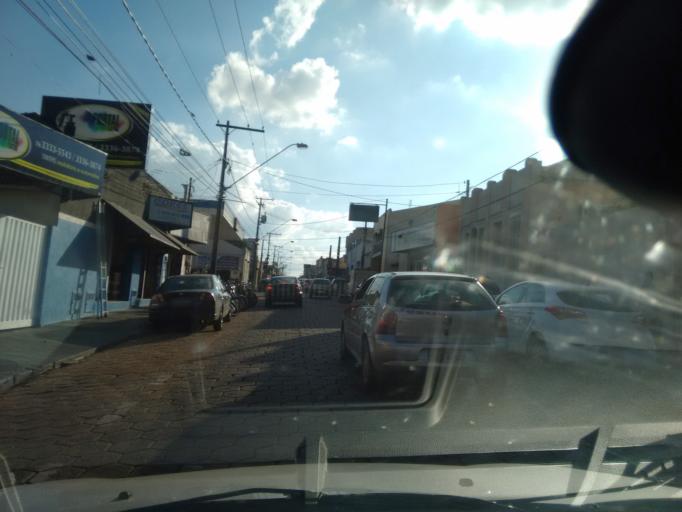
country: BR
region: Sao Paulo
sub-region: Araraquara
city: Araraquara
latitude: -21.7983
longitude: -48.1768
